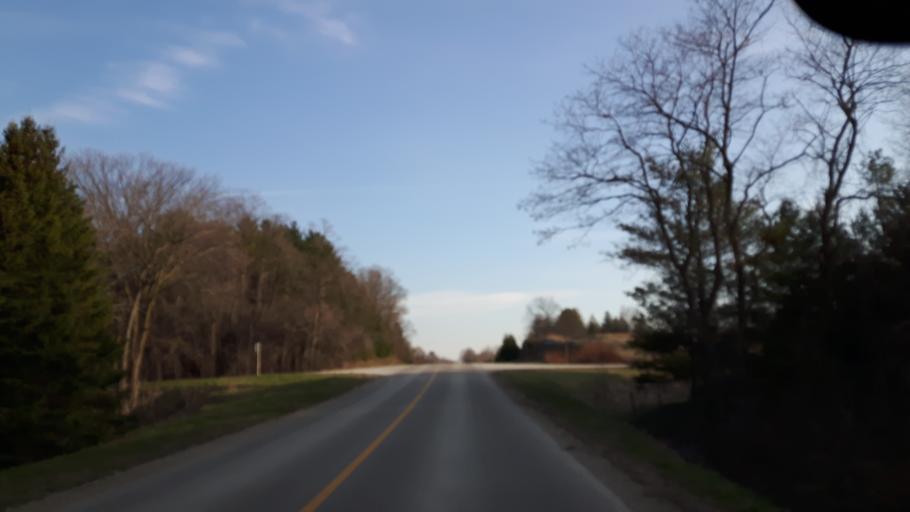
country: CA
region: Ontario
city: Goderich
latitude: 43.6621
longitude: -81.6643
